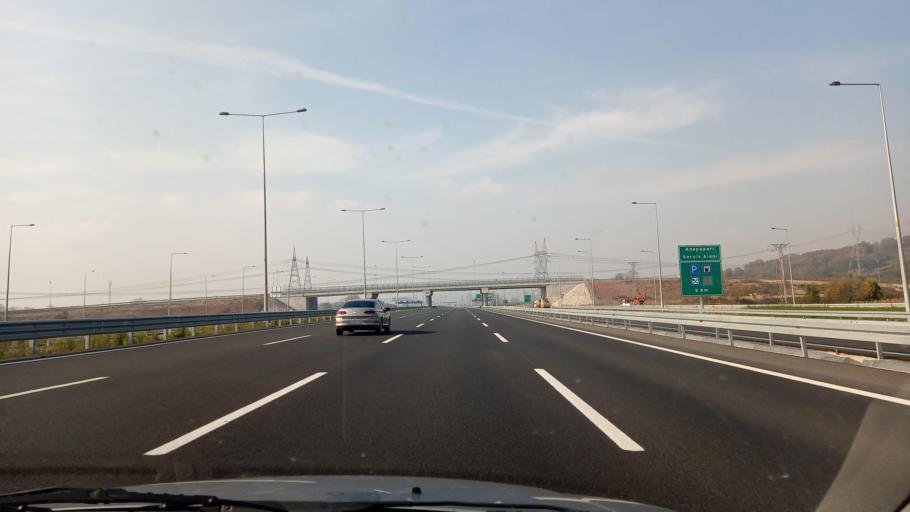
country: TR
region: Sakarya
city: Kazimpasa
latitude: 40.8416
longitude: 30.3499
